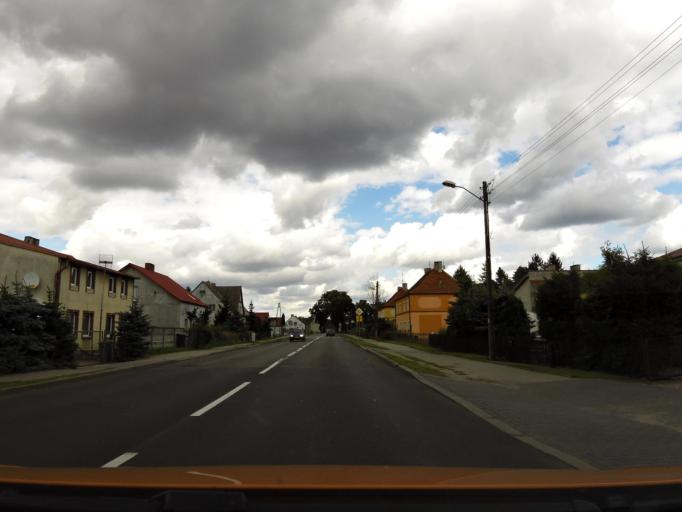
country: PL
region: West Pomeranian Voivodeship
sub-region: Powiat gryficki
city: Ploty
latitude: 53.7975
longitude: 15.2583
